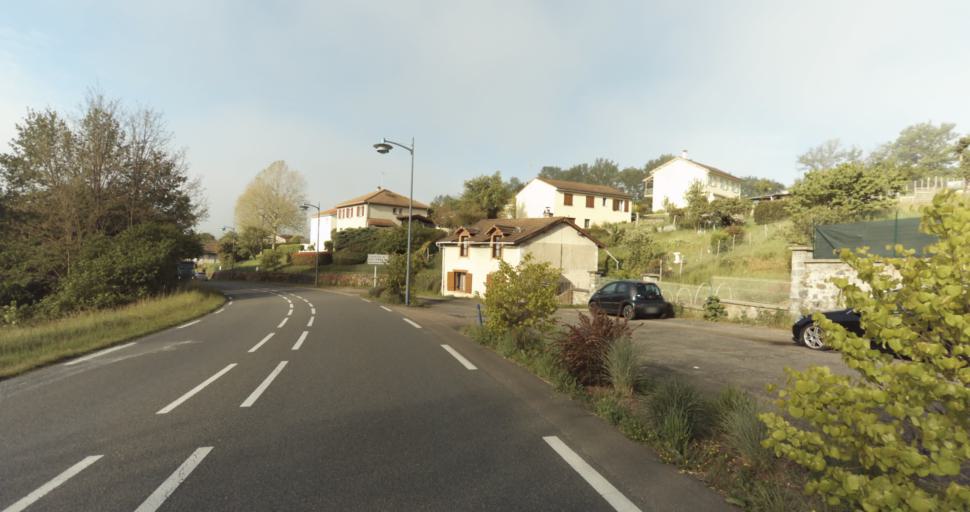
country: FR
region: Limousin
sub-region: Departement de la Haute-Vienne
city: Le Vigen
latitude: 45.7541
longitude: 1.2902
